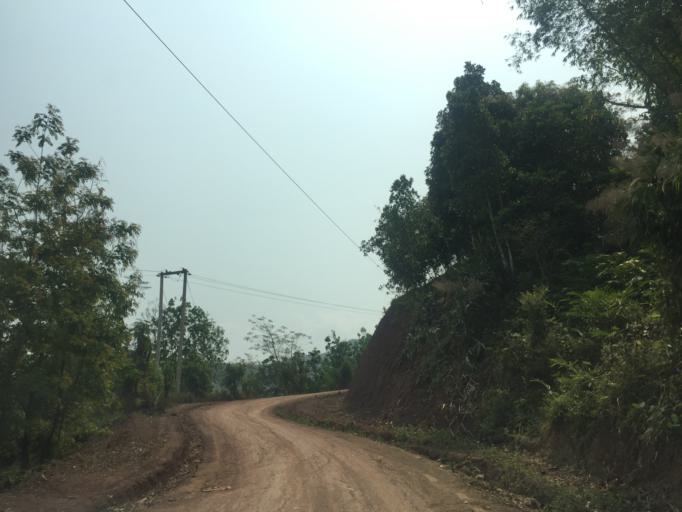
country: LA
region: Loungnamtha
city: Muang Nale
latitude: 20.3001
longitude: 101.6605
